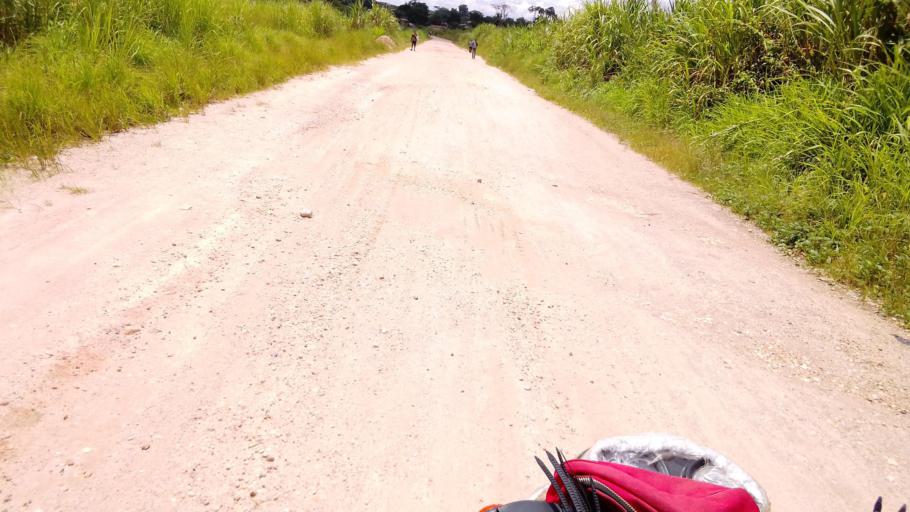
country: SL
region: Eastern Province
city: Koidu
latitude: 8.6731
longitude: -10.9924
